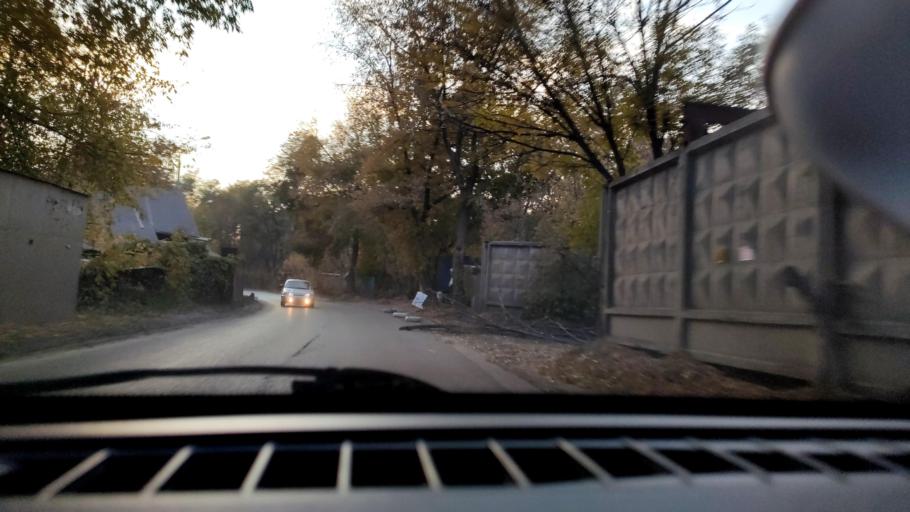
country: RU
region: Samara
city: Samara
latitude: 53.2027
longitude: 50.2497
